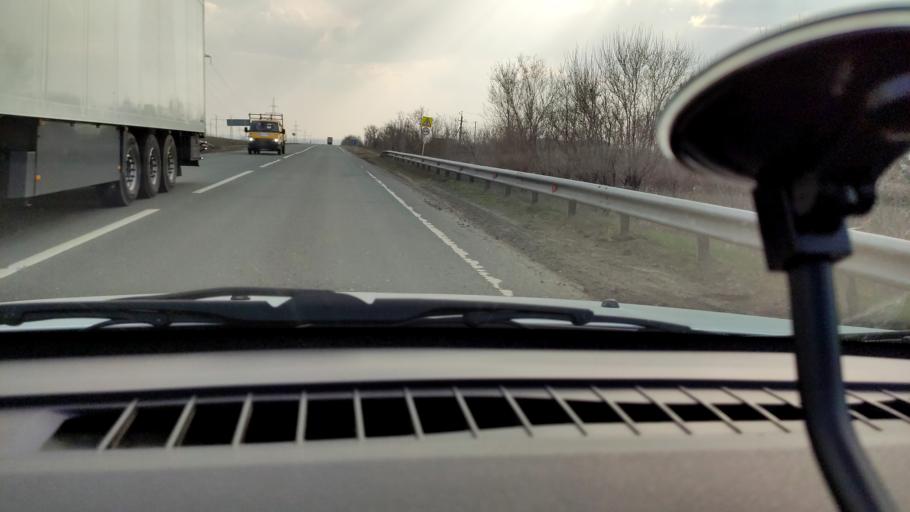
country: RU
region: Samara
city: Dubovyy Umet
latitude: 53.0733
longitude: 50.3840
